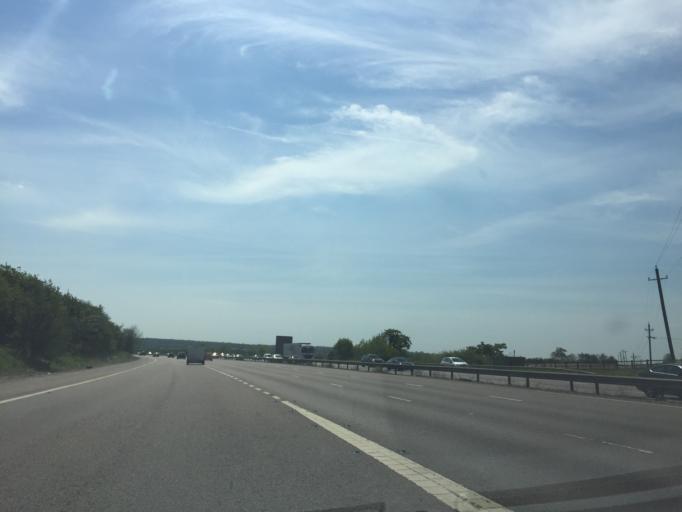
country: GB
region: England
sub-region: Essex
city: Harlow
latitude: 51.7386
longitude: 0.1368
